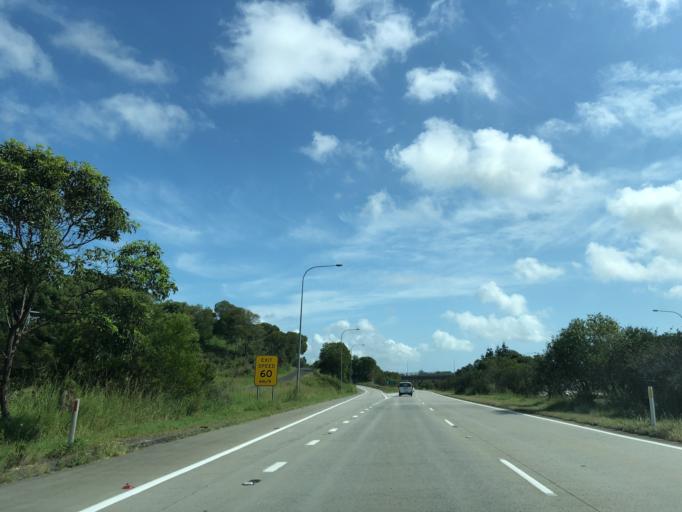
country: AU
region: New South Wales
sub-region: Byron Shire
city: Brunswick Heads
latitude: -28.5878
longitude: 153.5444
